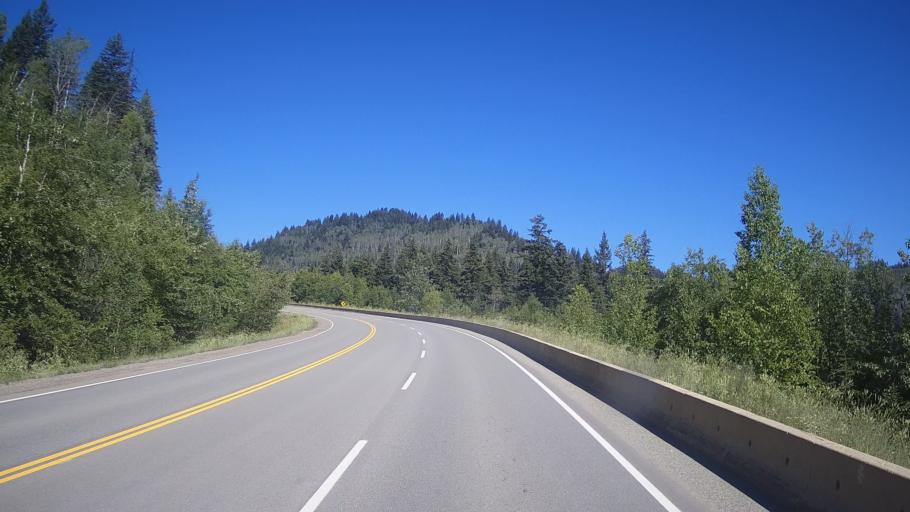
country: CA
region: British Columbia
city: Kamloops
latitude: 51.4940
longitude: -120.2717
